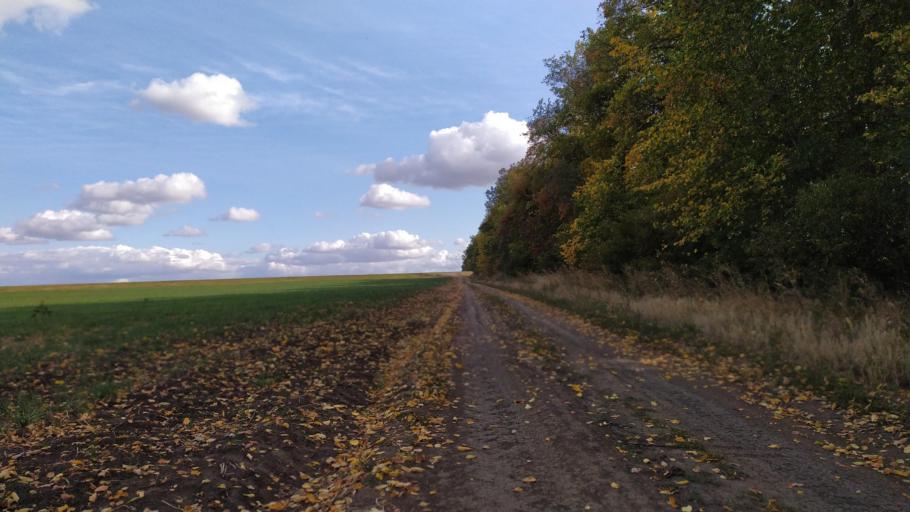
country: RU
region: Kursk
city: Kursk
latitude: 51.6178
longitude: 36.1635
